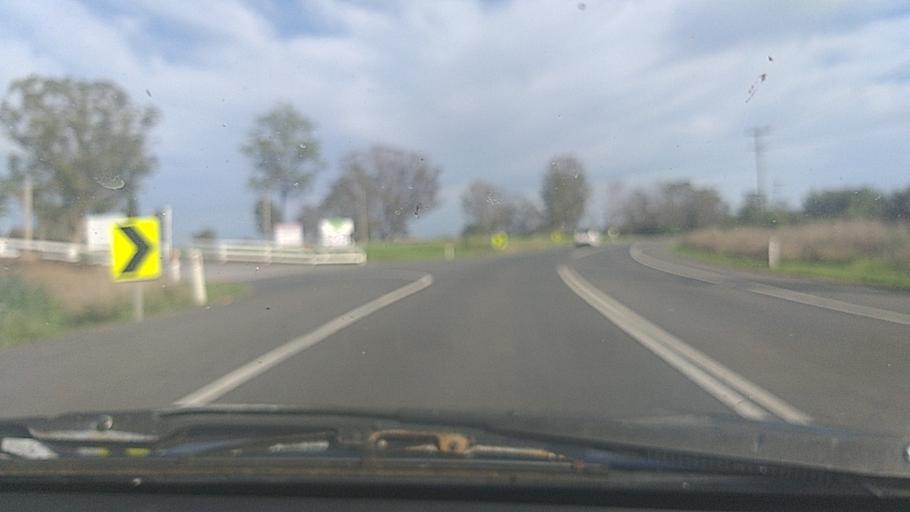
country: AU
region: New South Wales
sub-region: Liverpool
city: Bringelly
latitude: -33.9147
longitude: 150.7054
